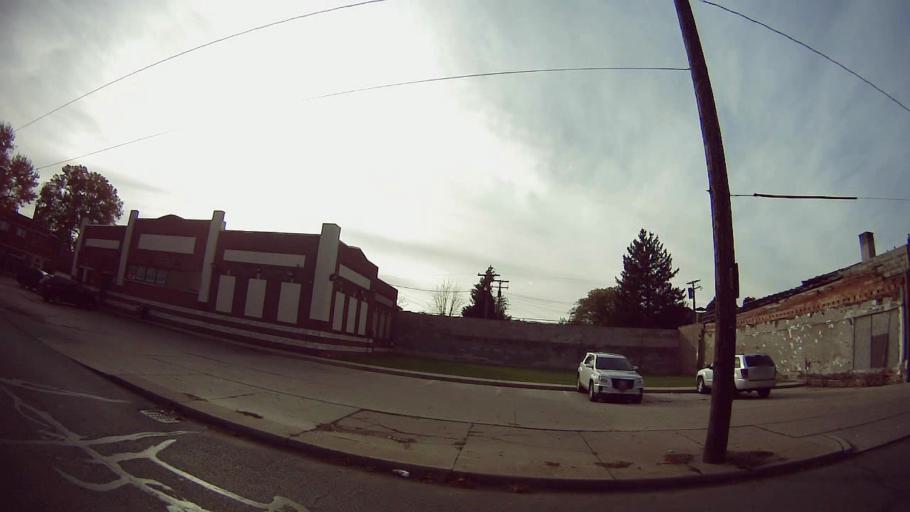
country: US
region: Michigan
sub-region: Wayne County
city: Highland Park
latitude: 42.4173
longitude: -83.1335
